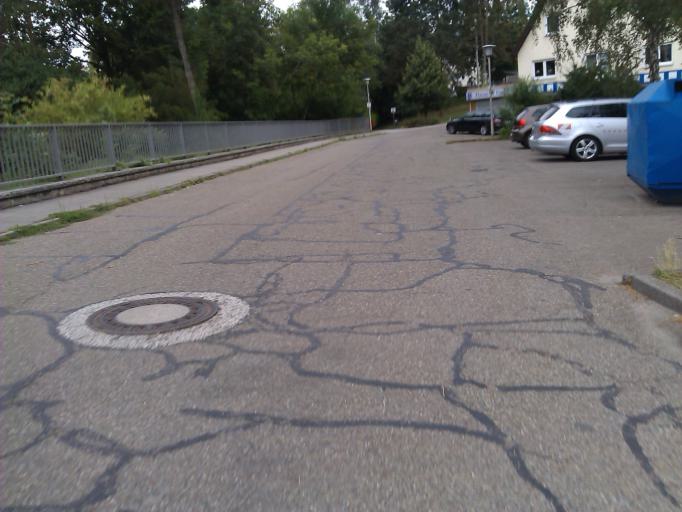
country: DE
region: Baden-Wuerttemberg
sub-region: Regierungsbezirk Stuttgart
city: Talheim
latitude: 49.0815
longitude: 9.1963
